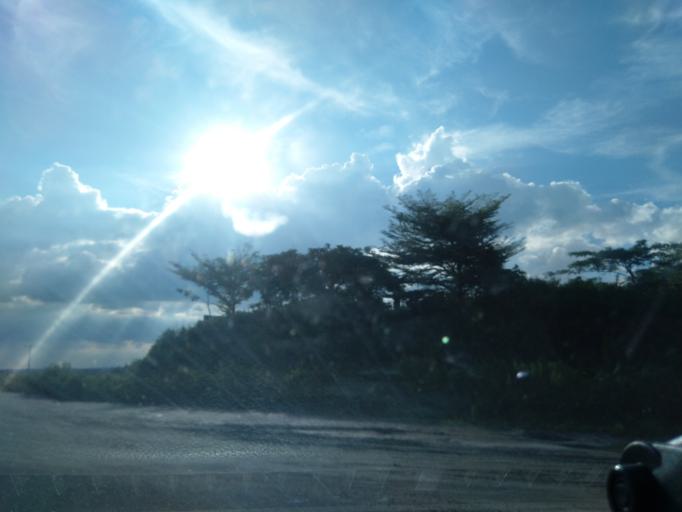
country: NG
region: Abuja Federal Capital Territory
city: Abuja
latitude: 9.0304
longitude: 7.3942
